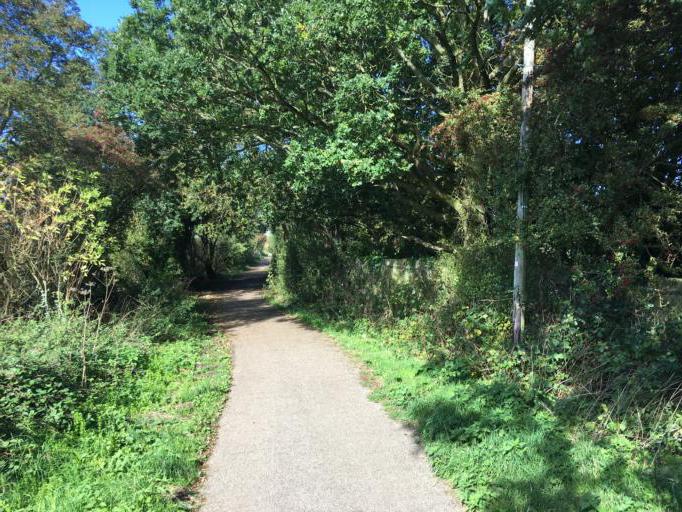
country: GB
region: England
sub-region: Warwickshire
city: Kenilworth
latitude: 52.3671
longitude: -1.5827
